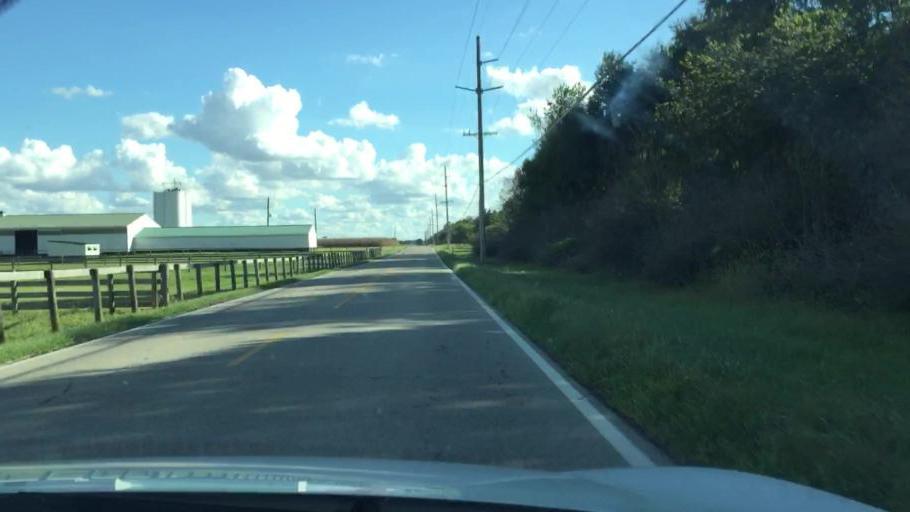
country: US
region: Ohio
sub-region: Clark County
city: Northridge
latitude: 39.9632
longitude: -83.7080
